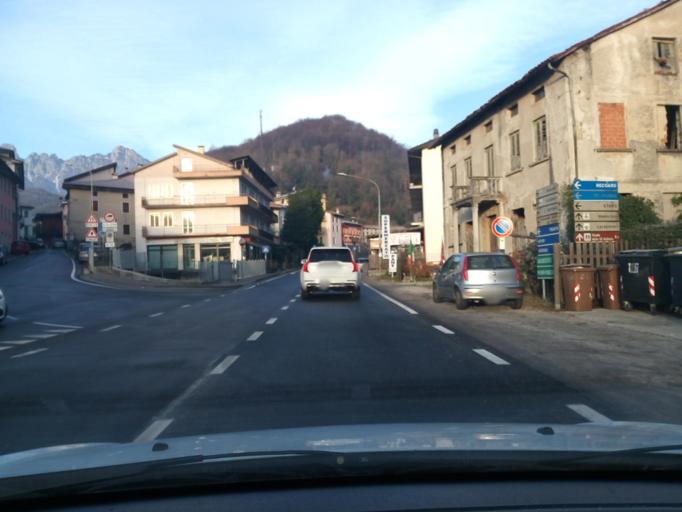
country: IT
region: Veneto
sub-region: Provincia di Vicenza
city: Valli del Pasubio
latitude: 45.7399
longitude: 11.2625
